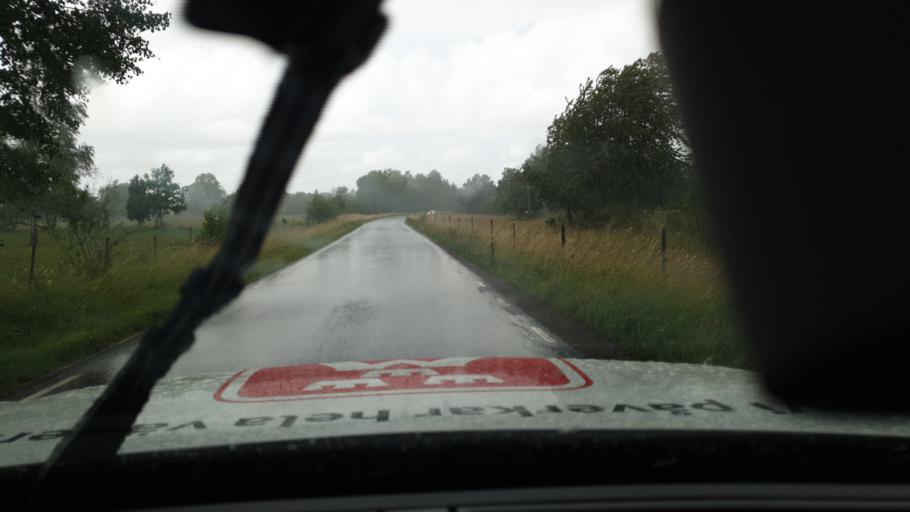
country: SE
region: Vaestra Goetaland
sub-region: Falkopings Kommun
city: Akarp
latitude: 58.2292
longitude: 13.6048
